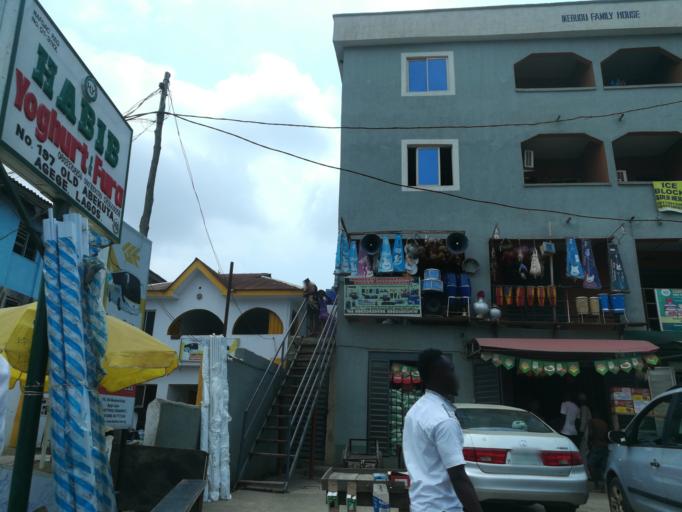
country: NG
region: Lagos
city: Agege
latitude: 6.6258
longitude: 3.3231
